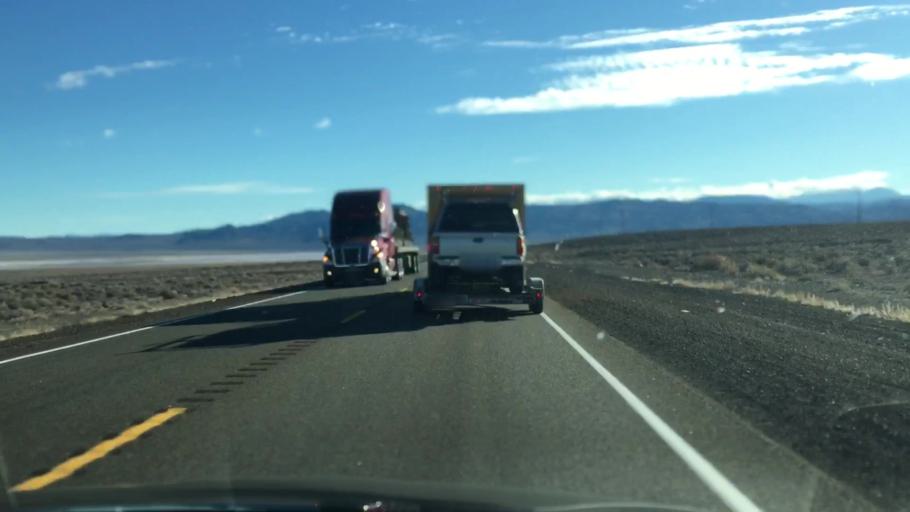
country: US
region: Nevada
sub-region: Mineral County
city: Hawthorne
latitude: 38.3333
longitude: -118.1031
